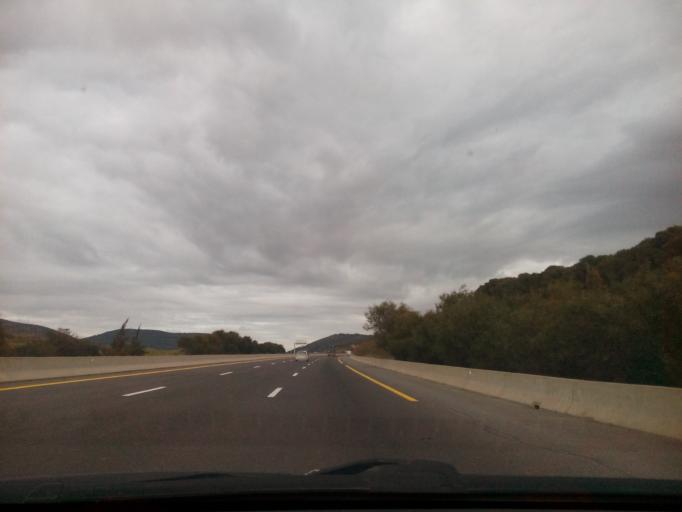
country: DZ
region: Sidi Bel Abbes
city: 'Ain el Berd
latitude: 35.3553
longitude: -0.5111
